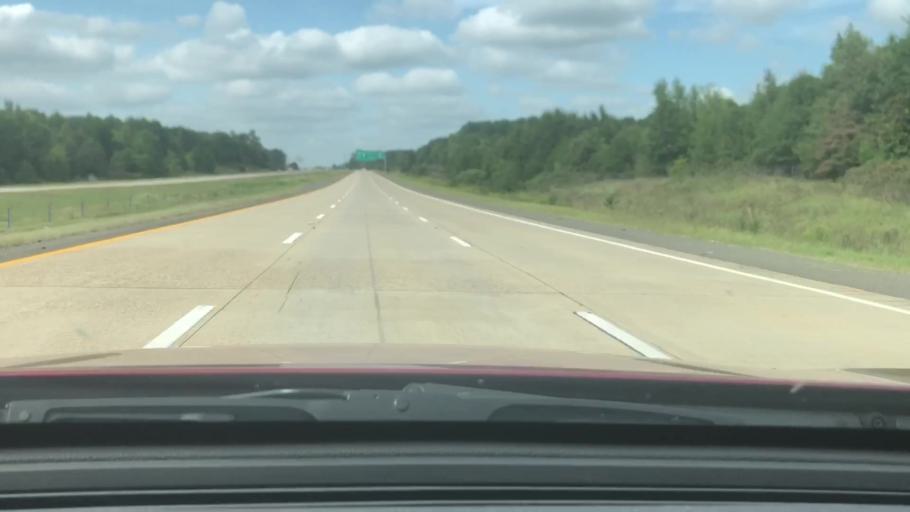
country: US
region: Texas
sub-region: Bowie County
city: Texarkana
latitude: 33.3650
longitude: -94.0068
